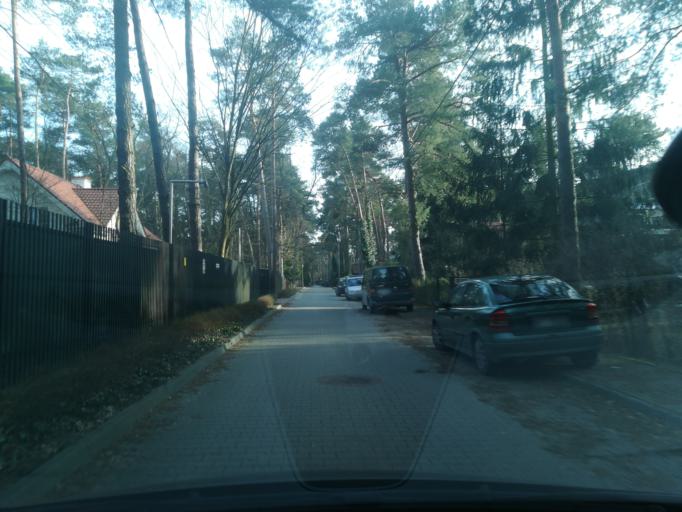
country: PL
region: Masovian Voivodeship
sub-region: Powiat piaseczynski
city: Konstancin-Jeziorna
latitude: 52.0762
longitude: 21.1075
